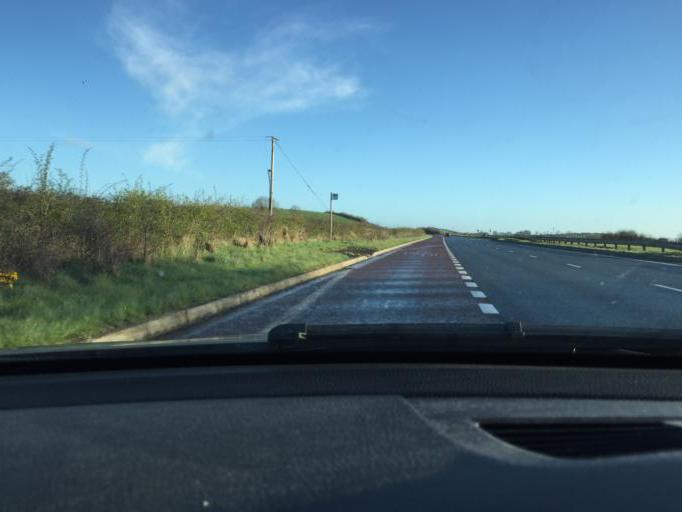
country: GB
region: Northern Ireland
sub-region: Banbridge District
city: Banbridge
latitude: 54.2978
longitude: -6.2981
